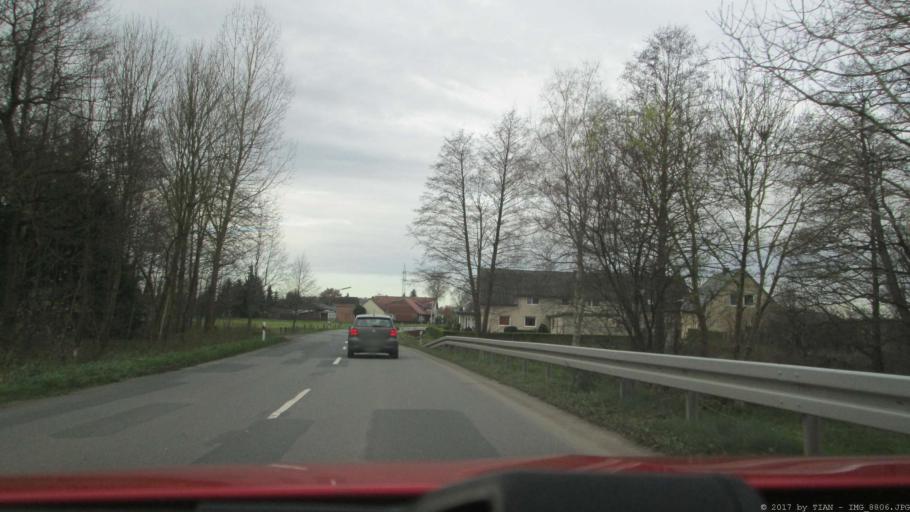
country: DE
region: Lower Saxony
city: Tiddische
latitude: 52.5187
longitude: 10.7977
